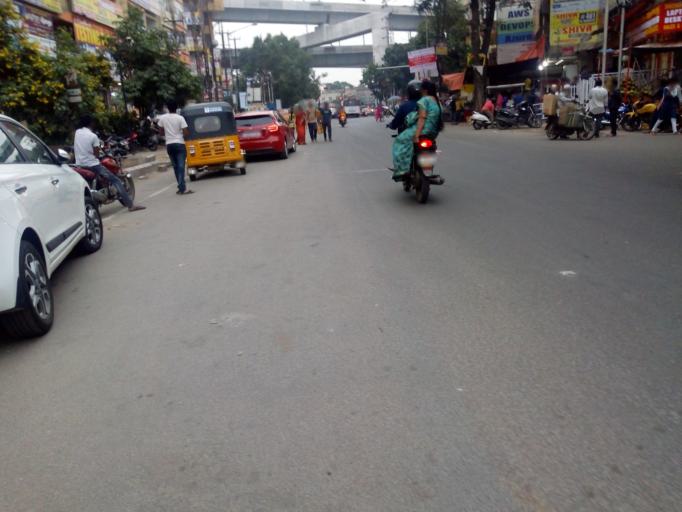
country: IN
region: Telangana
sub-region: Hyderabad
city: Hyderabad
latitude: 17.4370
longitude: 78.4454
